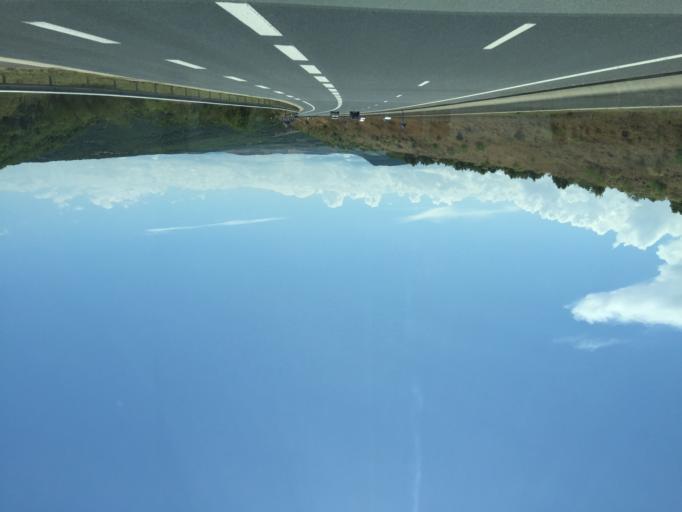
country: FR
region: Midi-Pyrenees
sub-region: Departement de l'Aveyron
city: Severac-le-Chateau
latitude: 44.2174
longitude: 3.0722
